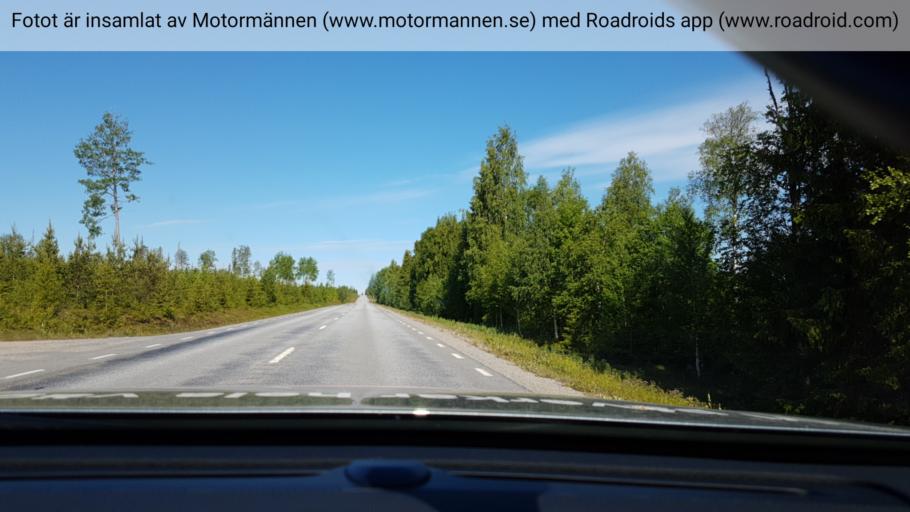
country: SE
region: Vaesterbotten
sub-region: Bjurholms Kommun
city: Bjurholm
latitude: 63.9471
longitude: 18.9067
